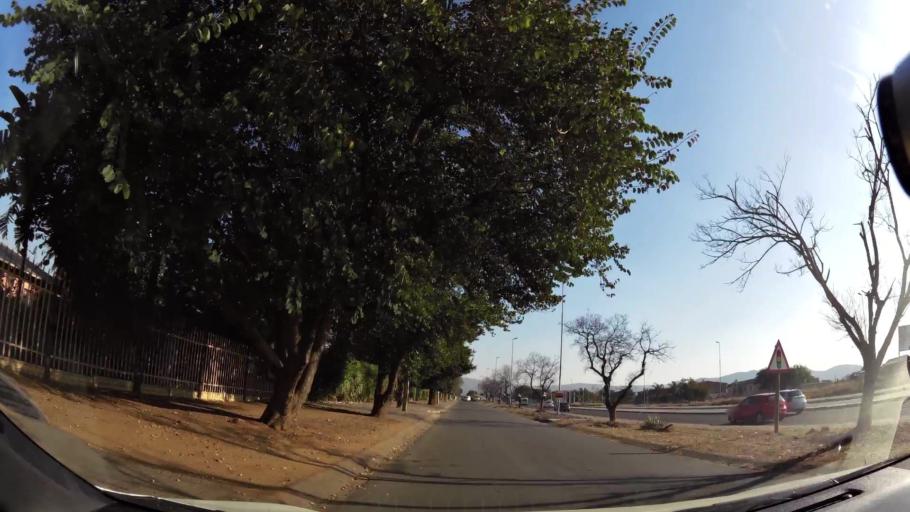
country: ZA
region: North-West
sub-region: Bojanala Platinum District Municipality
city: Rustenburg
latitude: -25.6508
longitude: 27.2512
